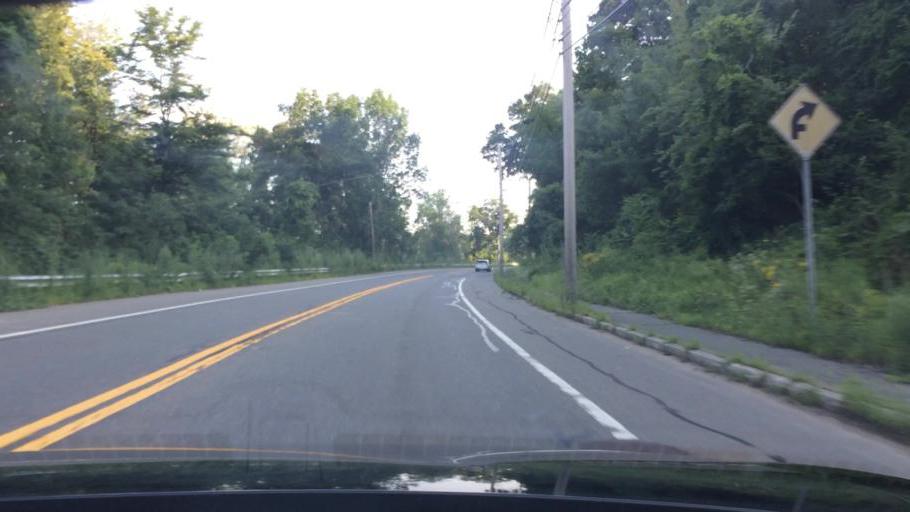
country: US
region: Massachusetts
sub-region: Essex County
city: Haverhill
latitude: 42.7667
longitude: -71.1314
